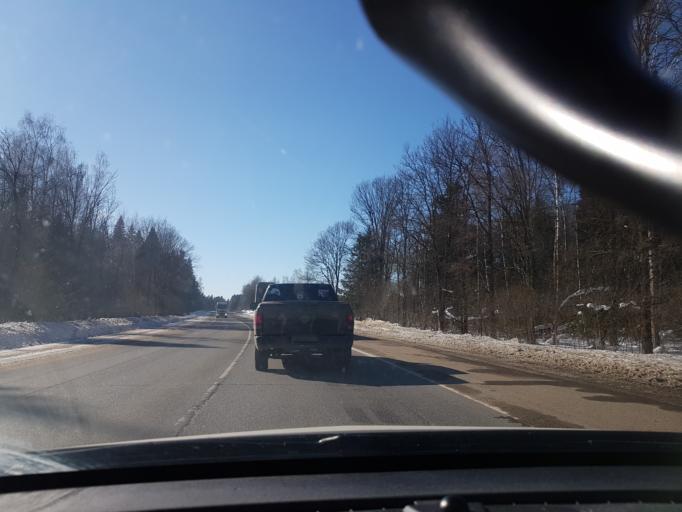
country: RU
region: Moskovskaya
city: Kostrovo
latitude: 55.9143
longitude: 36.7356
